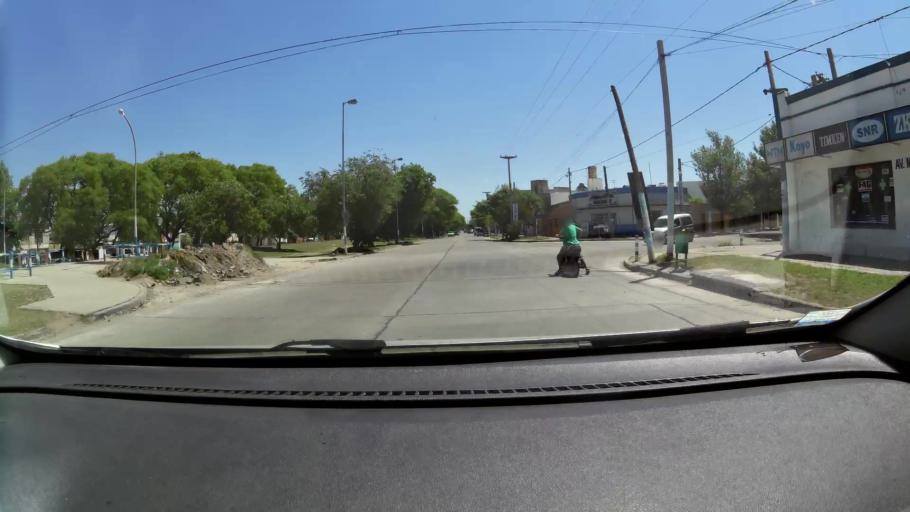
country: AR
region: Cordoba
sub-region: Departamento de Capital
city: Cordoba
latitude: -31.3940
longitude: -64.1543
